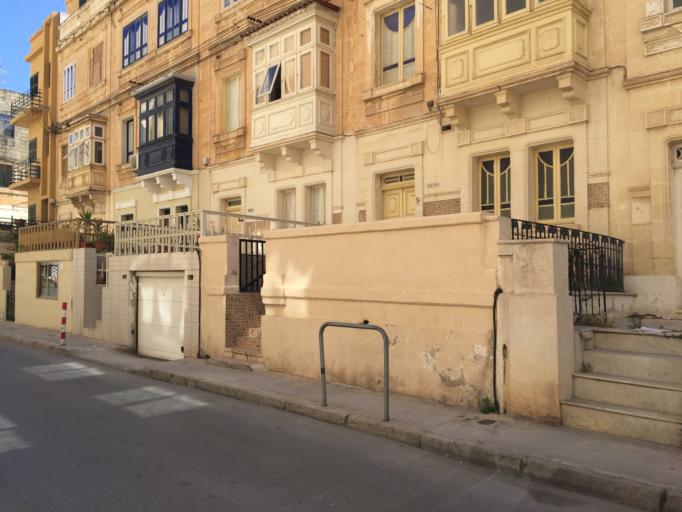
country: MT
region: Tas-Sliema
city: Sliema
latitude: 35.9131
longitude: 14.4962
